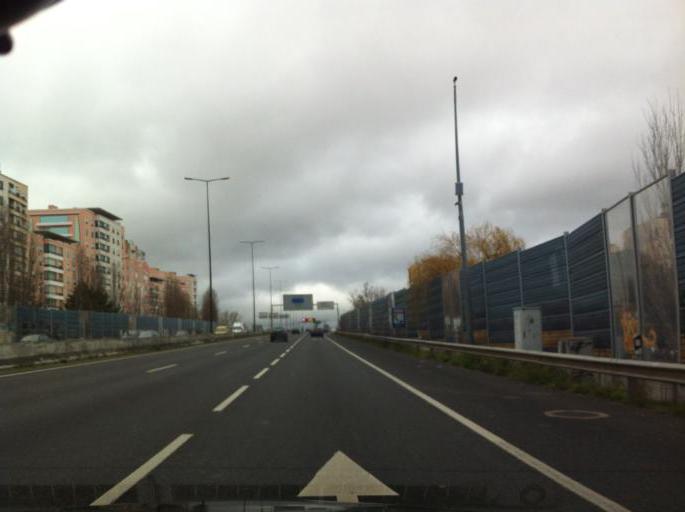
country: PT
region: Lisbon
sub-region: Odivelas
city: Pontinha
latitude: 38.7603
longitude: -9.1729
